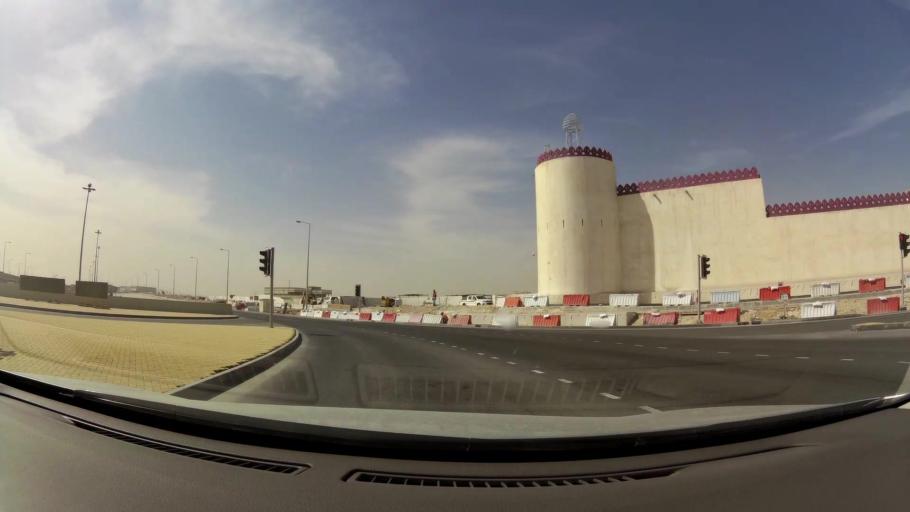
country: QA
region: Baladiyat ar Rayyan
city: Ar Rayyan
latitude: 25.3006
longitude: 51.4300
